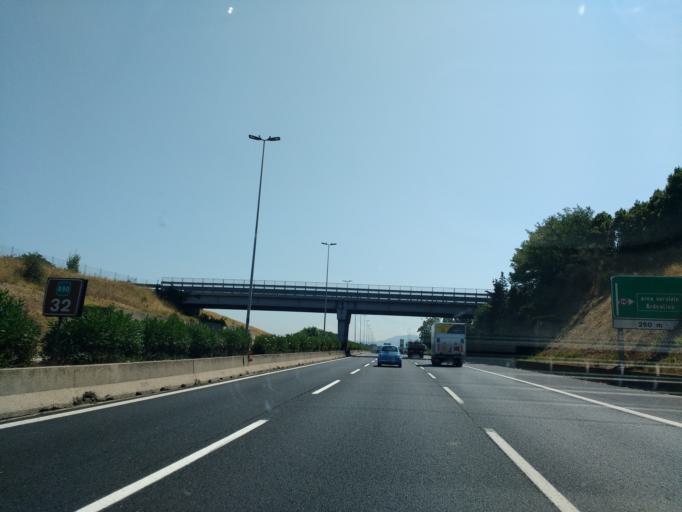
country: IT
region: Latium
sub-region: Citta metropolitana di Roma Capitale
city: Selcetta
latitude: 41.7942
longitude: 12.5129
